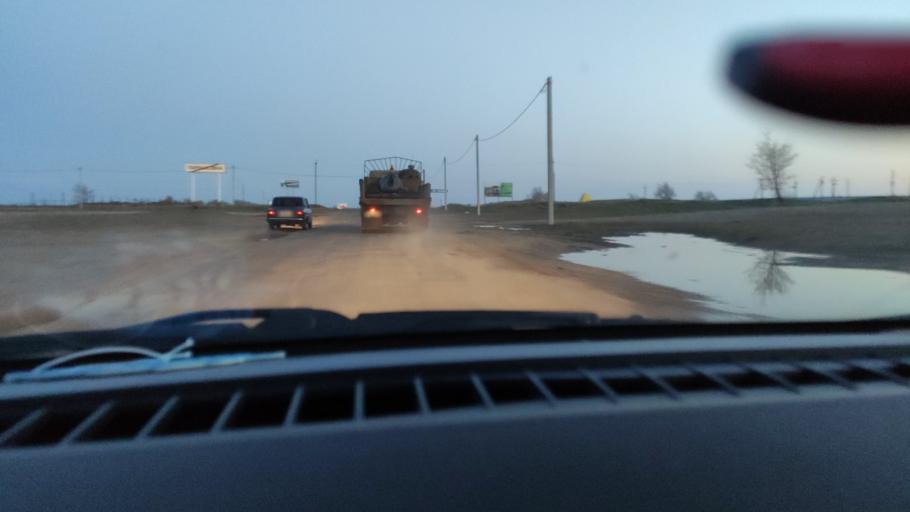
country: RU
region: Saratov
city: Rovnoye
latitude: 51.0195
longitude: 46.0934
